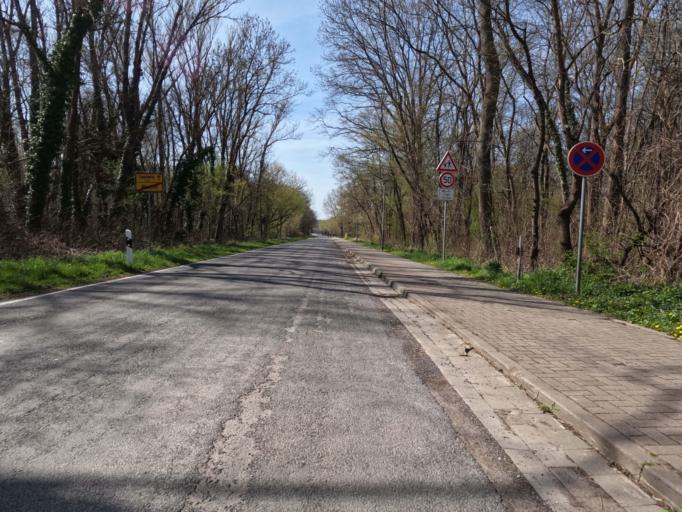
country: DE
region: Saxony-Anhalt
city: Wettin
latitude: 51.5807
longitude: 11.8119
